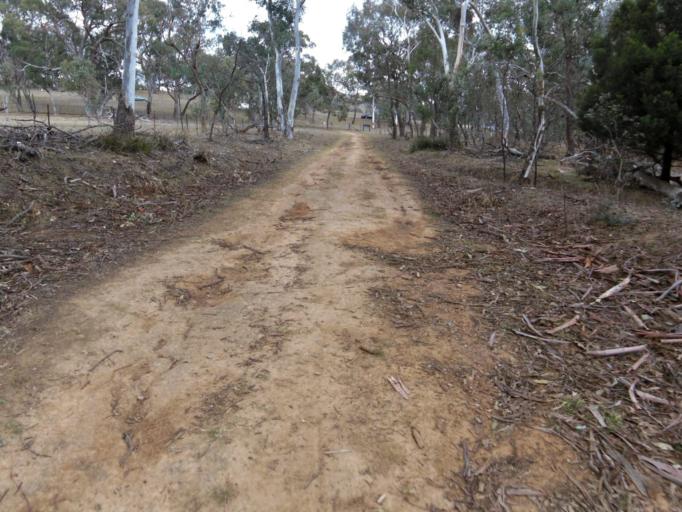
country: AU
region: Australian Capital Territory
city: Macquarie
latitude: -35.2717
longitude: 149.0769
